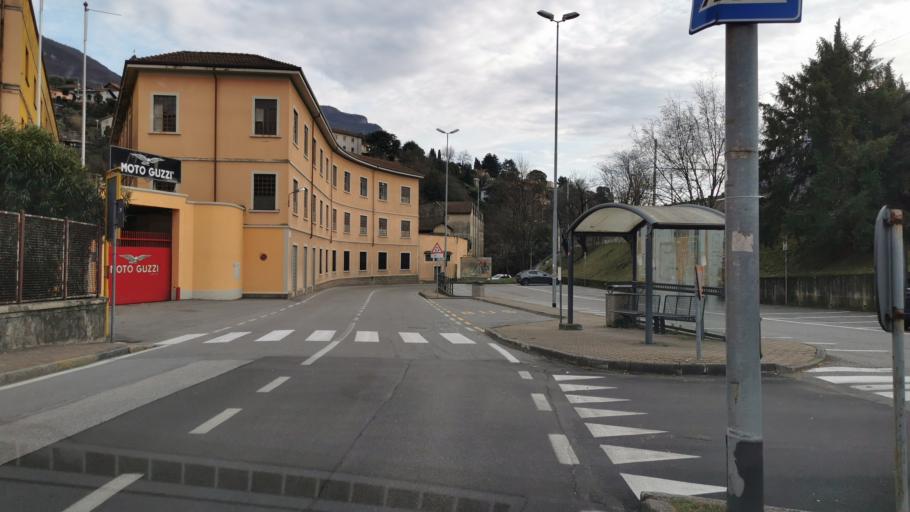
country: IT
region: Lombardy
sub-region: Provincia di Lecco
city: Mandello del Lario
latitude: 45.9153
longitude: 9.3226
